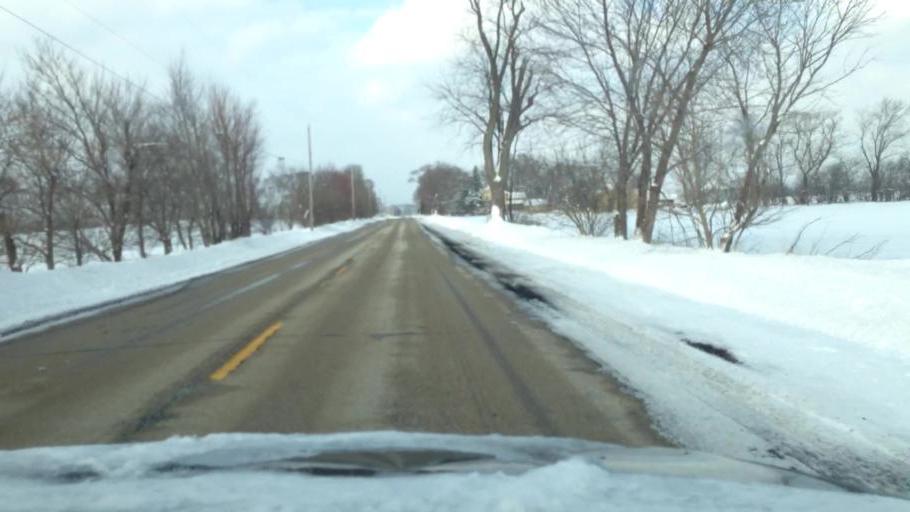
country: US
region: Wisconsin
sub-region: Walworth County
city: East Troy
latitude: 42.7842
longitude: -88.4450
